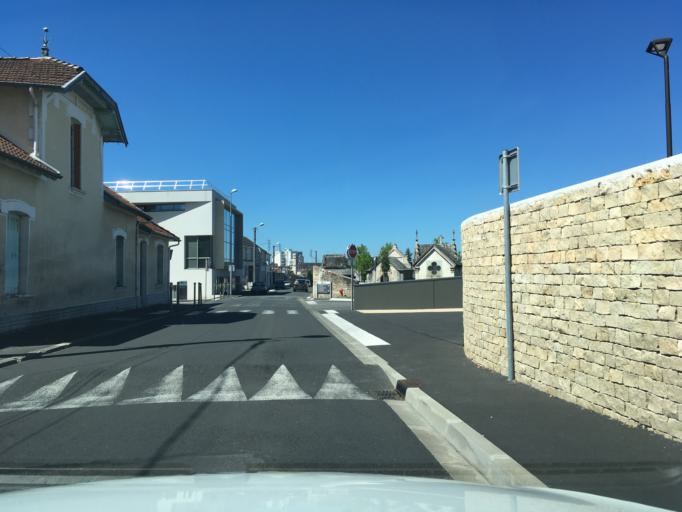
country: FR
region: Poitou-Charentes
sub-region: Departement des Deux-Sevres
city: Niort
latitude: 46.3251
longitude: -0.4494
